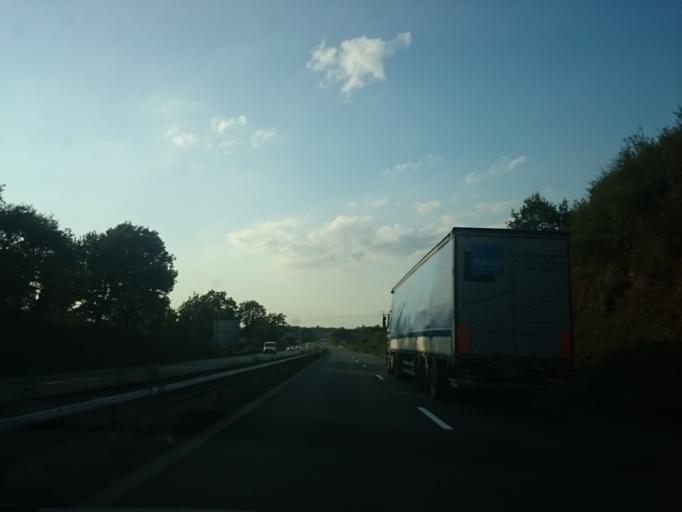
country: FR
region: Pays de la Loire
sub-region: Departement de la Loire-Atlantique
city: Pontchateau
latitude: 47.4329
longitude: -2.0667
